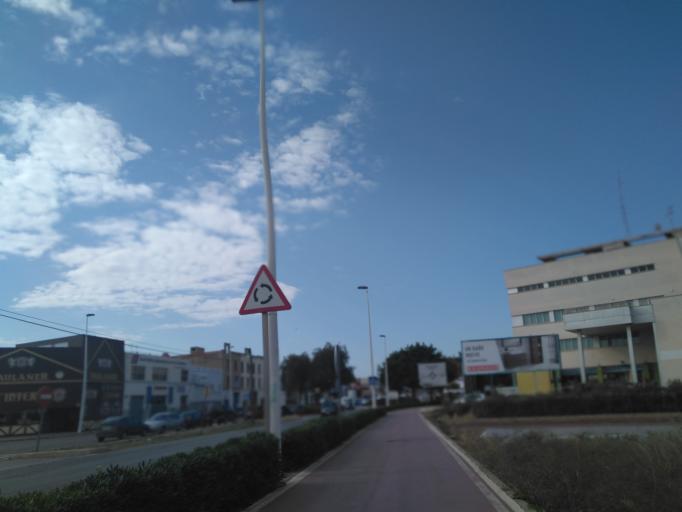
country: ES
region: Valencia
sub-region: Provincia de Valencia
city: Alboraya
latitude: 39.5023
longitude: -0.3460
